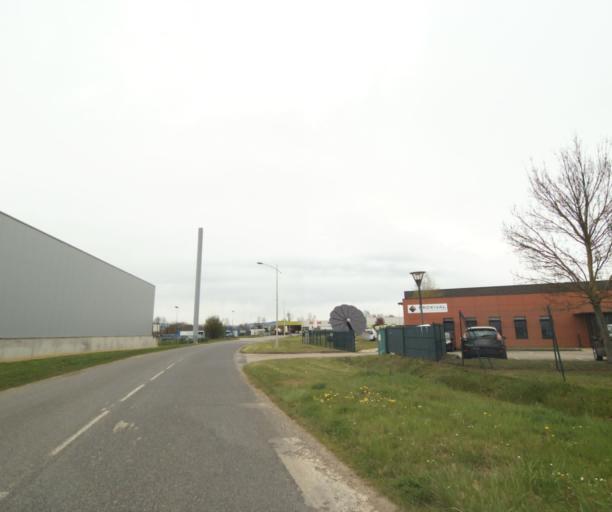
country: FR
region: Bourgogne
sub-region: Departement de Saone-et-Loire
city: Charnay-les-Macon
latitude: 46.2893
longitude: 4.7810
